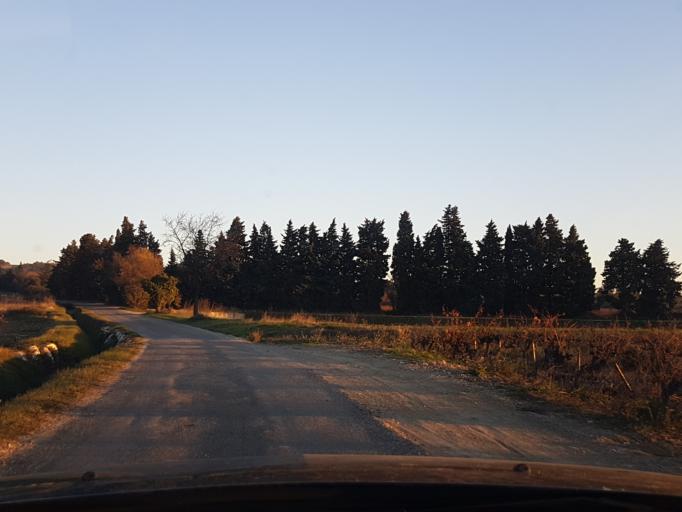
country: FR
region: Provence-Alpes-Cote d'Azur
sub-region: Departement du Vaucluse
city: Vedene
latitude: 43.9647
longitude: 4.9057
